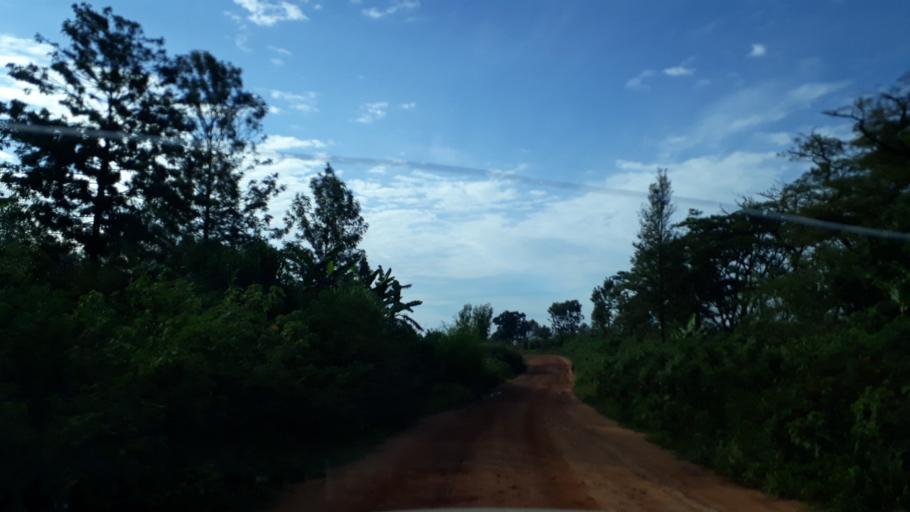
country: UG
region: Northern Region
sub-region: Zombo District
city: Paidha
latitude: 2.2566
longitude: 30.8961
